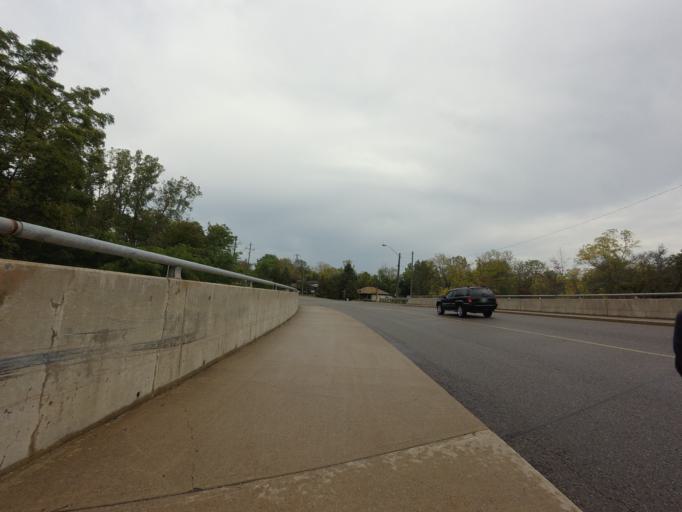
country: CA
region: Ontario
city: Brantford
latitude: 43.1373
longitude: -80.2215
